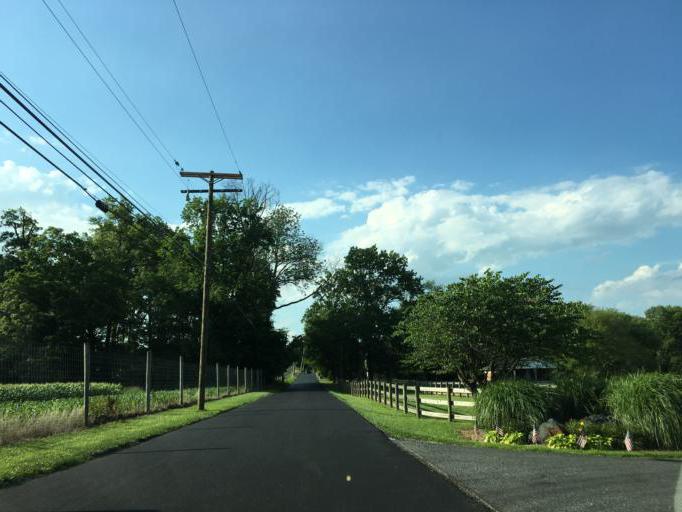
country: US
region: Maryland
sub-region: Baltimore County
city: Kingsville
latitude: 39.4527
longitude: -76.4384
